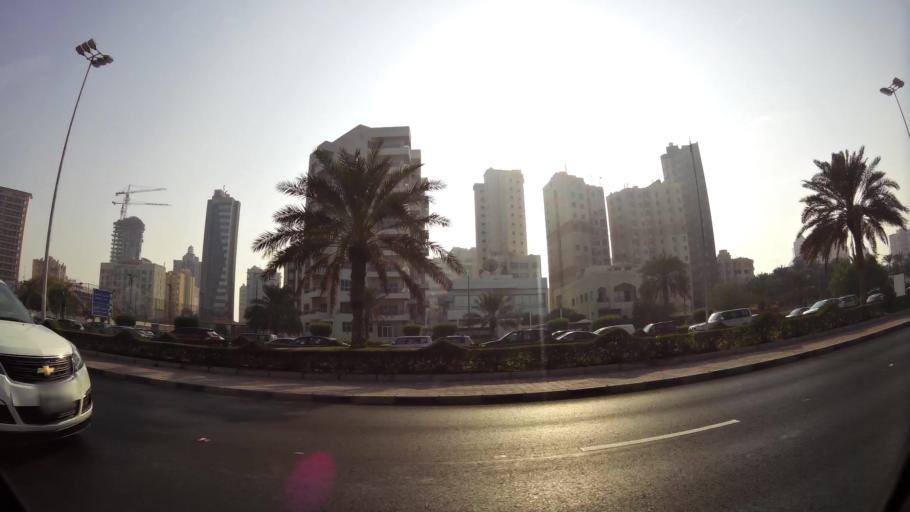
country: KW
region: Al Asimah
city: Ad Dasmah
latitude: 29.3713
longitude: 48.0094
